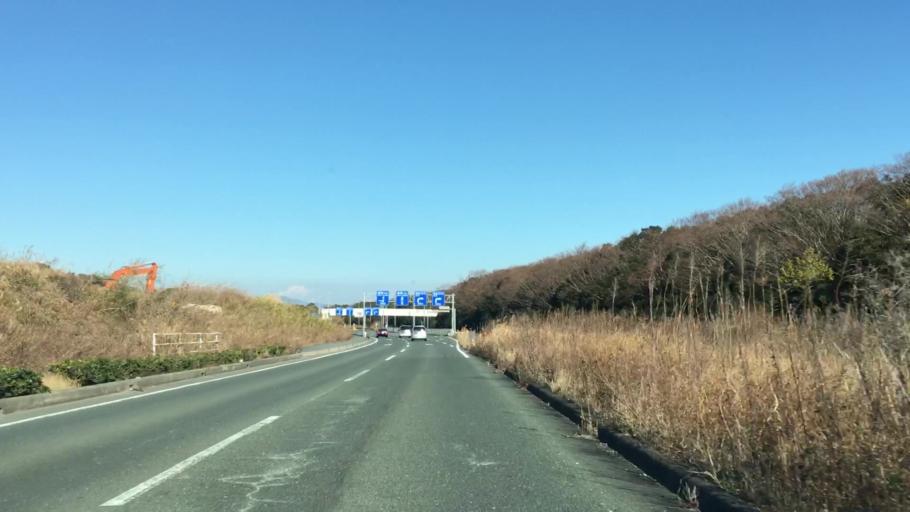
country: JP
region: Aichi
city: Tahara
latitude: 34.6956
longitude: 137.3240
